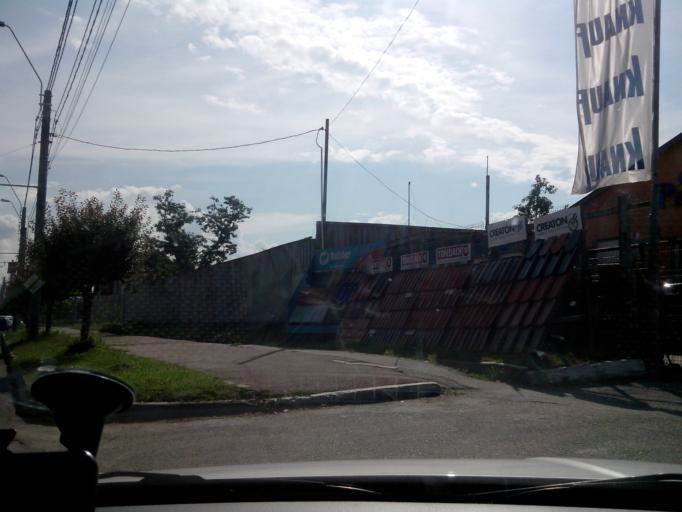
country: RO
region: Maramures
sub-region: Comuna Recea
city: Recea
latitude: 47.6469
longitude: 23.5371
